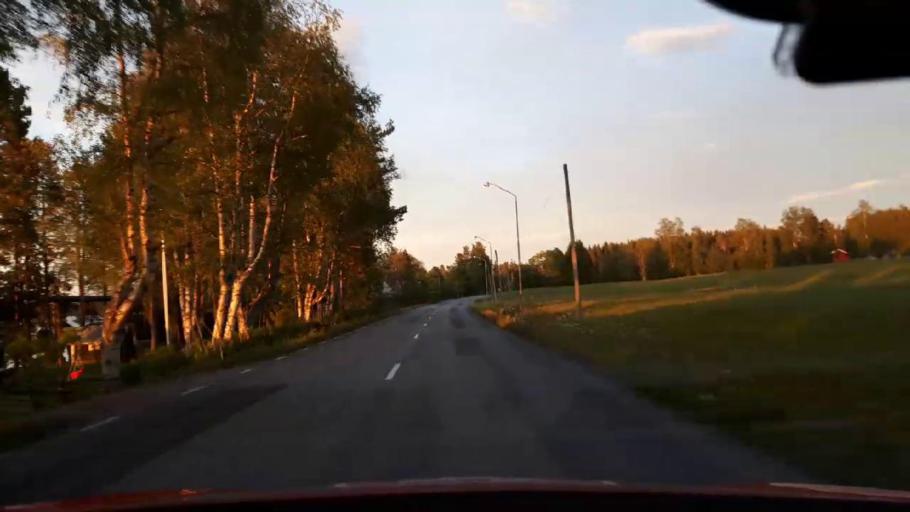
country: SE
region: Jaemtland
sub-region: OEstersunds Kommun
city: Ostersund
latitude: 63.1317
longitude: 14.6632
